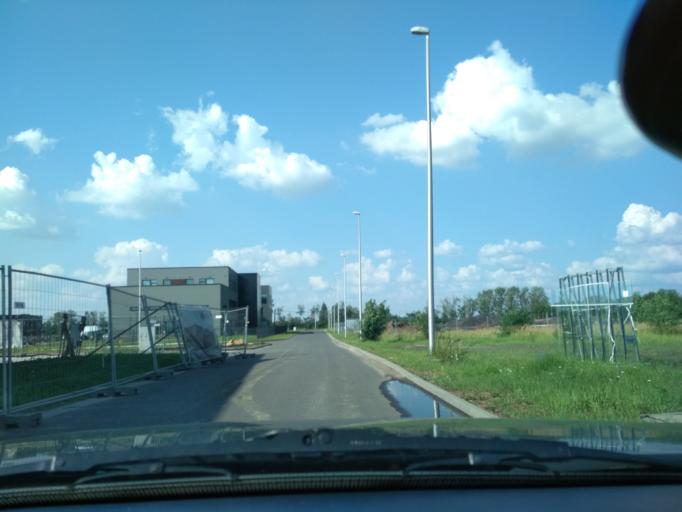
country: PL
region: Silesian Voivodeship
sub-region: Gliwice
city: Gliwice
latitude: 50.2771
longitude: 18.6877
